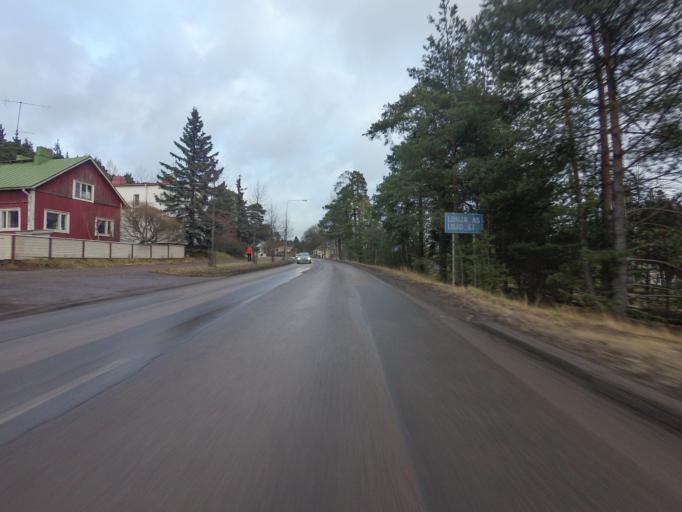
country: FI
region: Uusimaa
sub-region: Helsinki
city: Lohja
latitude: 60.2632
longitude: 24.1108
